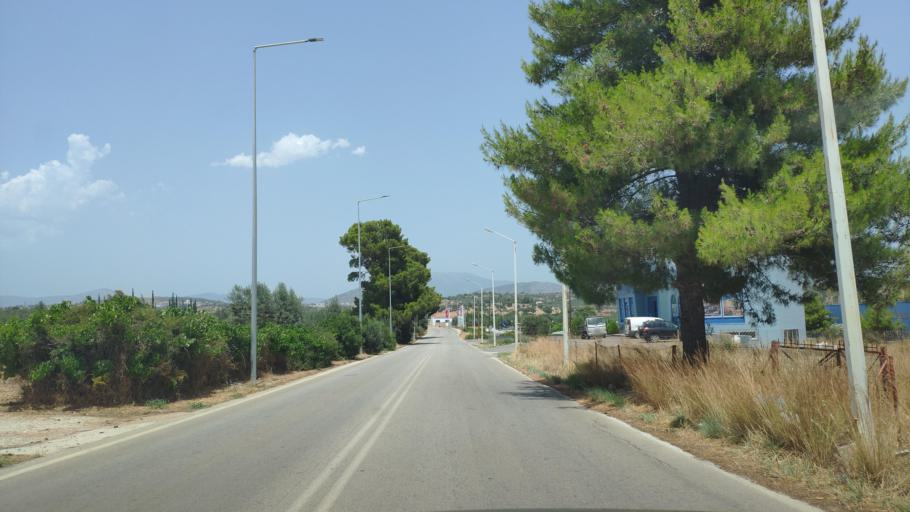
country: GR
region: Peloponnese
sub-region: Nomos Argolidos
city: Porto Cheli
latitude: 37.3405
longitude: 23.1568
